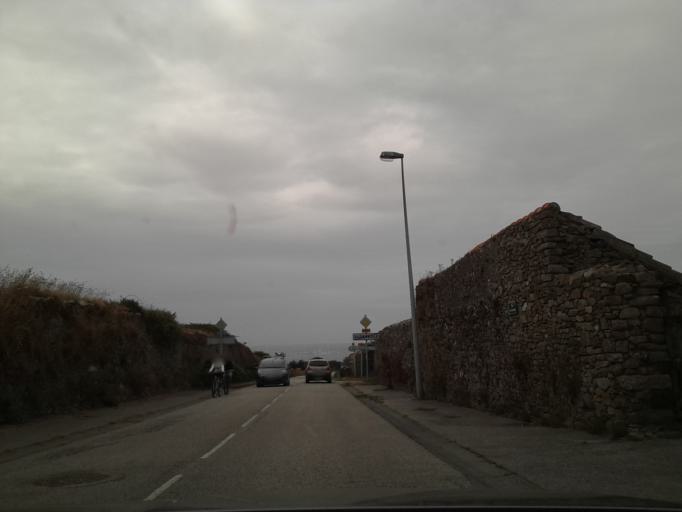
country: FR
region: Lower Normandy
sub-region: Departement de la Manche
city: Beaumont-Hague
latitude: 49.7137
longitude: -1.9315
